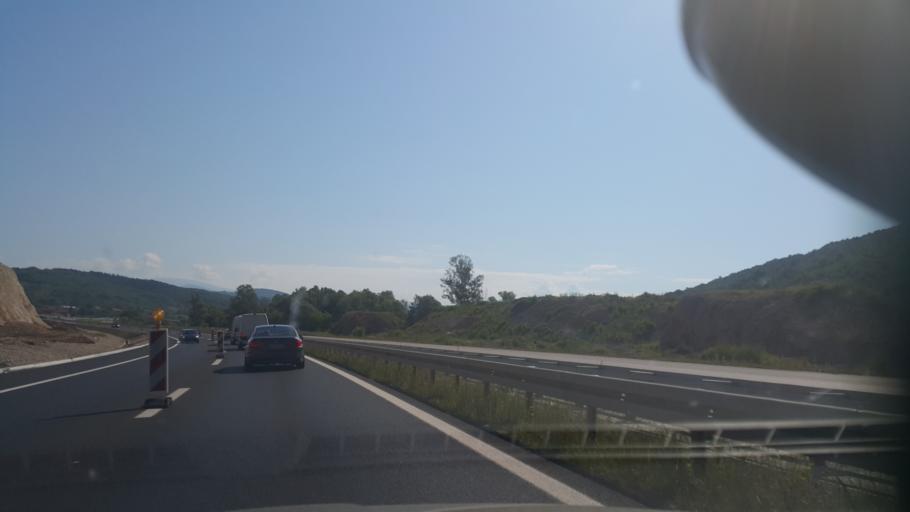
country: RS
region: Central Serbia
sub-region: Pirotski Okrug
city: Bela Palanka
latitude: 43.2236
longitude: 22.4276
